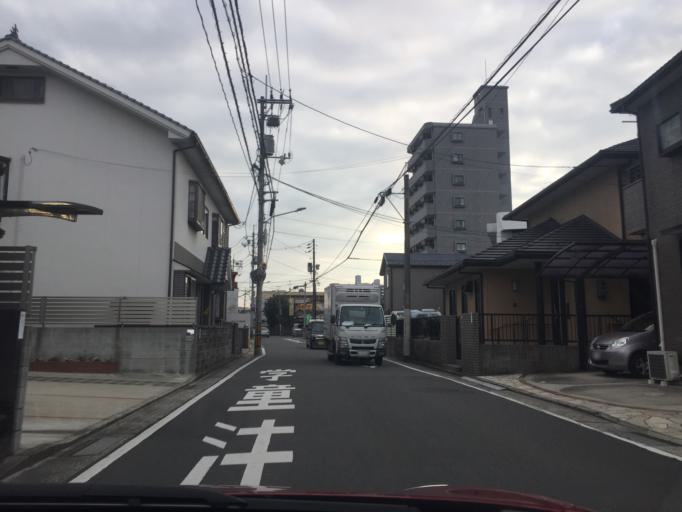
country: JP
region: Hiroshima
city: Hiroshima-shi
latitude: 34.4306
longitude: 132.4589
